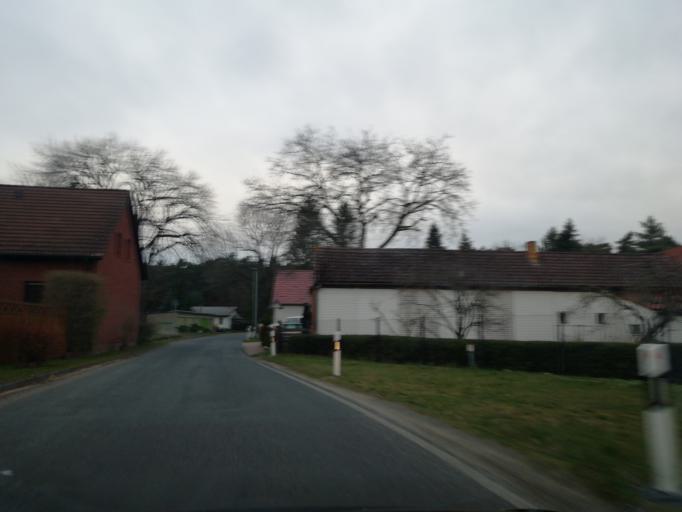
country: DE
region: Brandenburg
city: Vetschau
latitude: 51.7678
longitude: 14.0806
